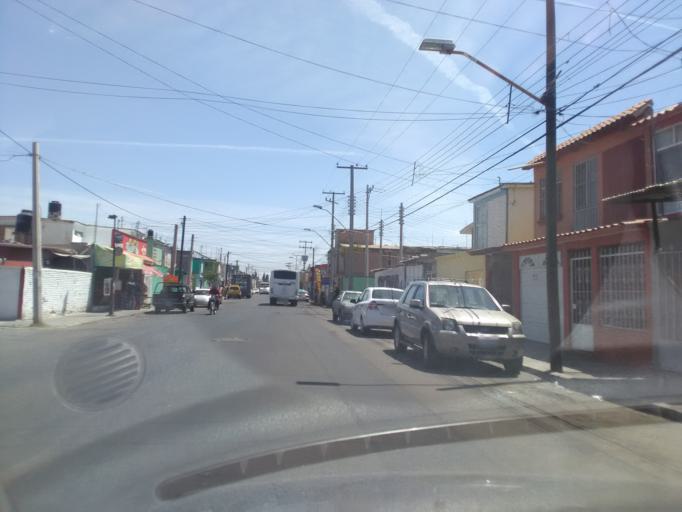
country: MX
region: Durango
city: Victoria de Durango
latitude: 24.0083
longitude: -104.6536
